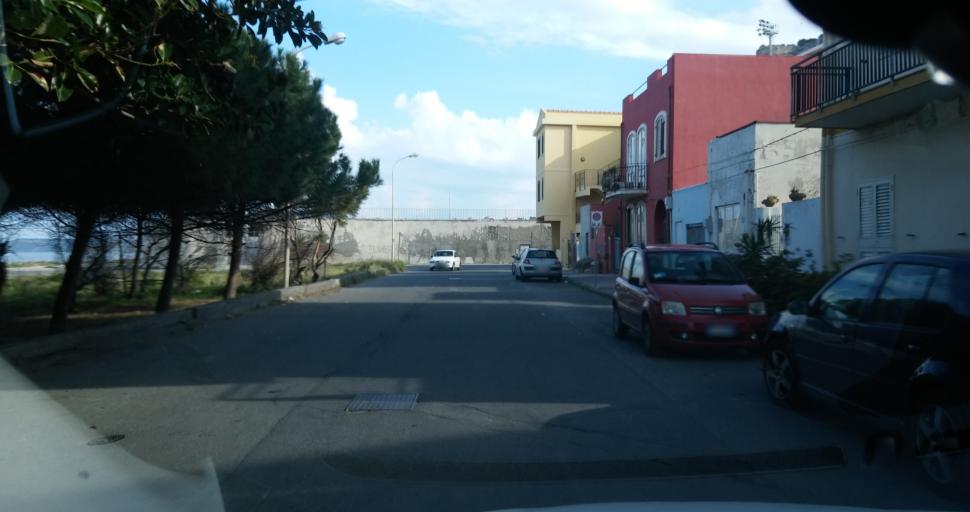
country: IT
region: Sicily
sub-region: Messina
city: Milazzo
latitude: 38.2295
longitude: 15.2376
